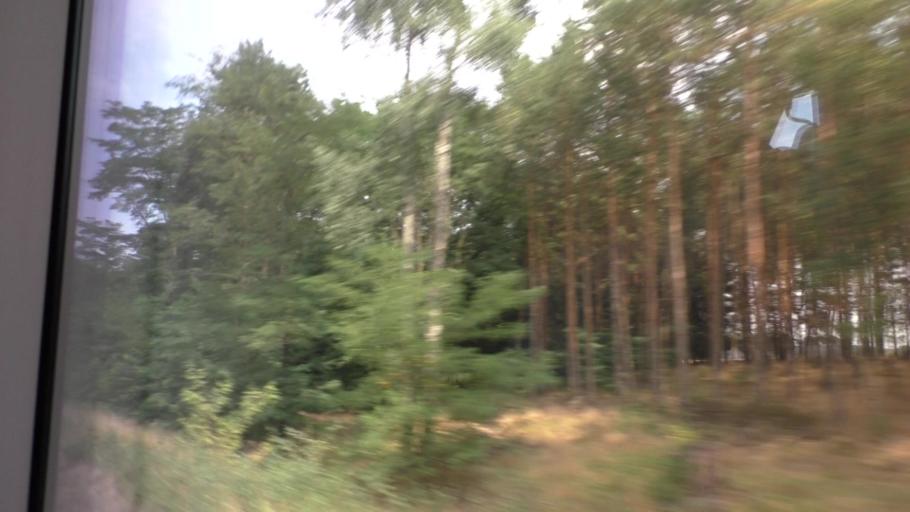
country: DE
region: Brandenburg
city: Mixdorf
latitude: 52.1831
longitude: 14.3852
